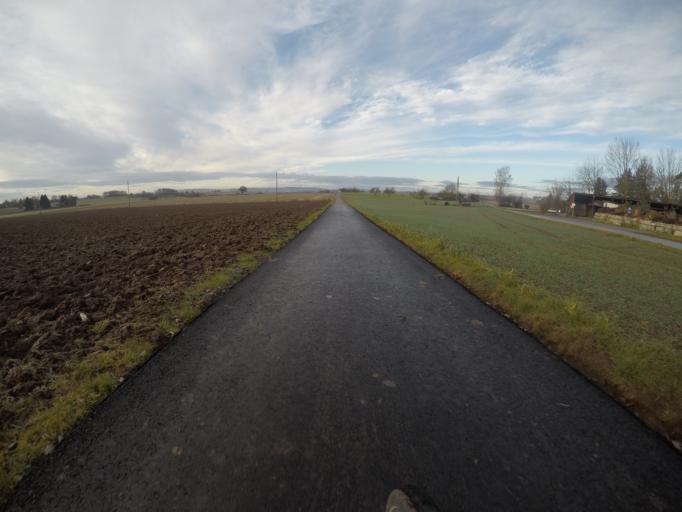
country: DE
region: Baden-Wuerttemberg
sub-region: Regierungsbezirk Stuttgart
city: Magstadt
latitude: 48.7081
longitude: 8.9749
